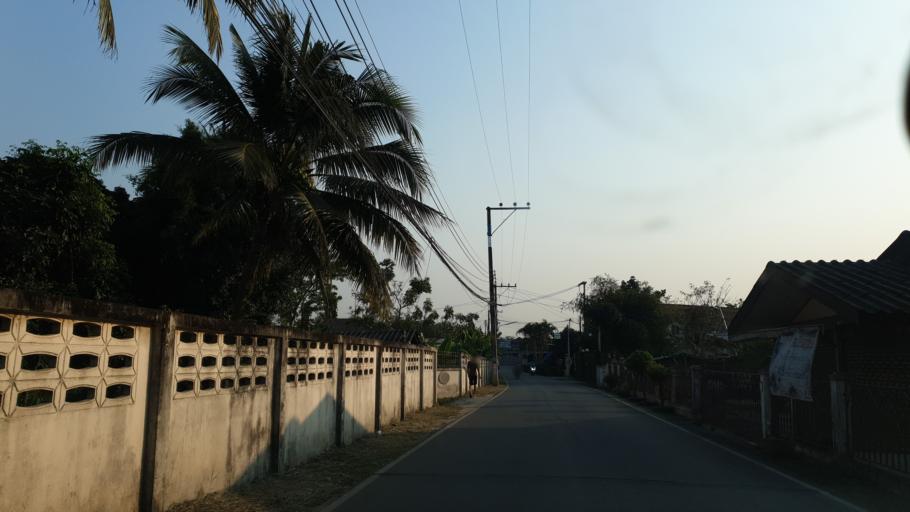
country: TH
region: Chiang Mai
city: Saraphi
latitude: 18.7156
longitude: 99.0262
